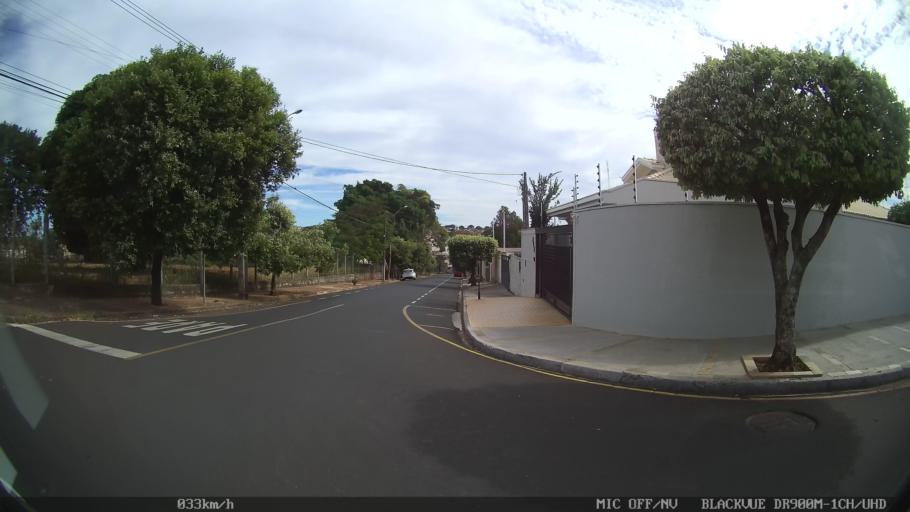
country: BR
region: Sao Paulo
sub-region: Catanduva
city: Catanduva
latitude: -21.1491
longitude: -48.9722
